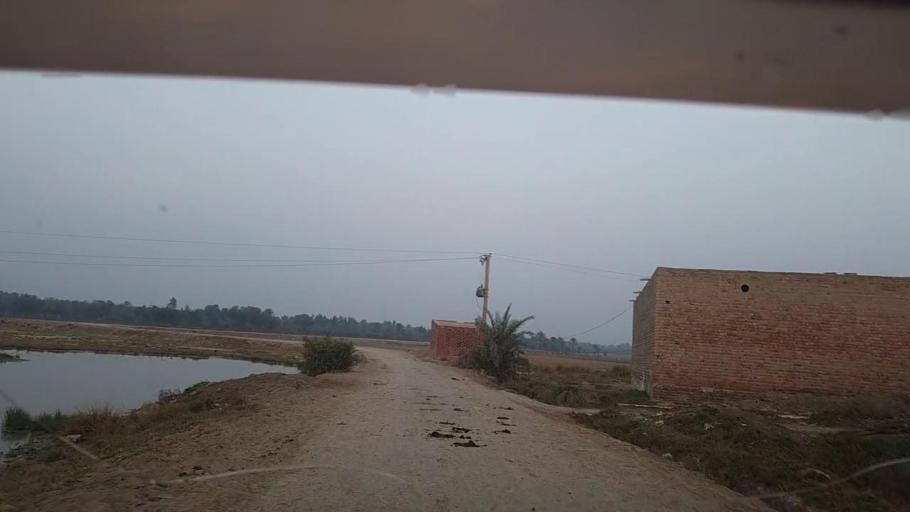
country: PK
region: Sindh
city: Khairpur
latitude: 27.5770
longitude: 68.7312
